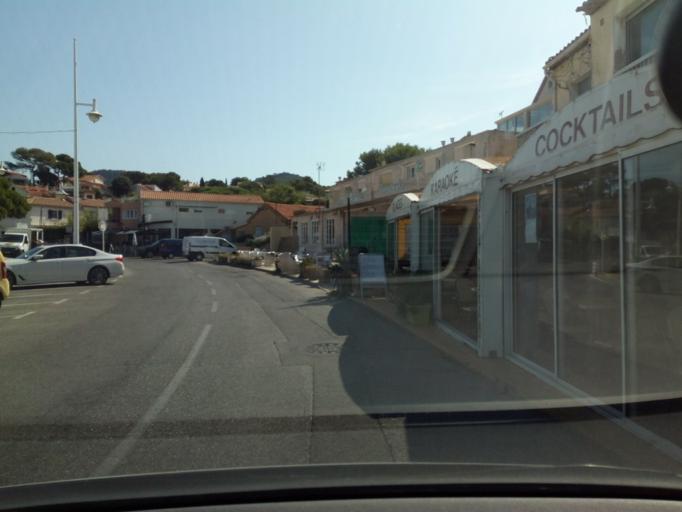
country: FR
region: Provence-Alpes-Cote d'Azur
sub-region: Departement du Var
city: Le Pradet
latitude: 43.0845
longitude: 6.0194
